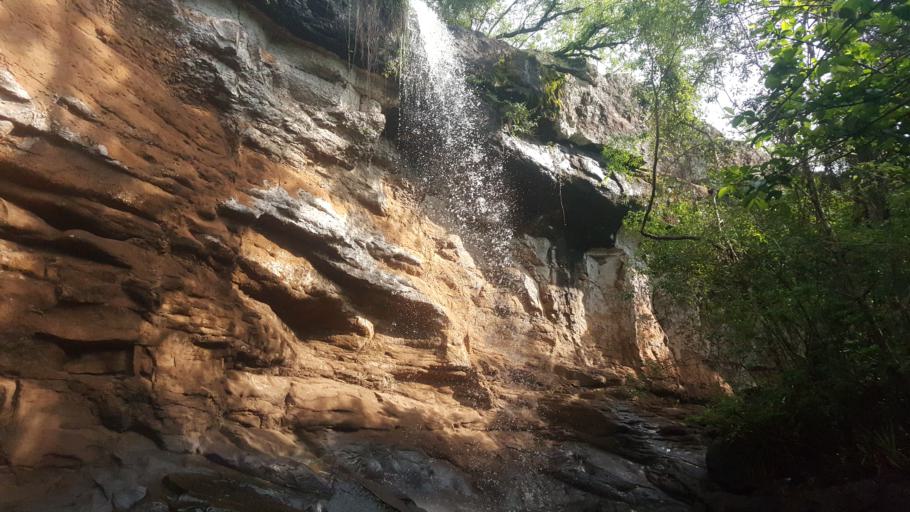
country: AR
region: Misiones
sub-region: Departamento de Candelaria
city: Candelaria
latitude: -27.5605
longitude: -55.7099
